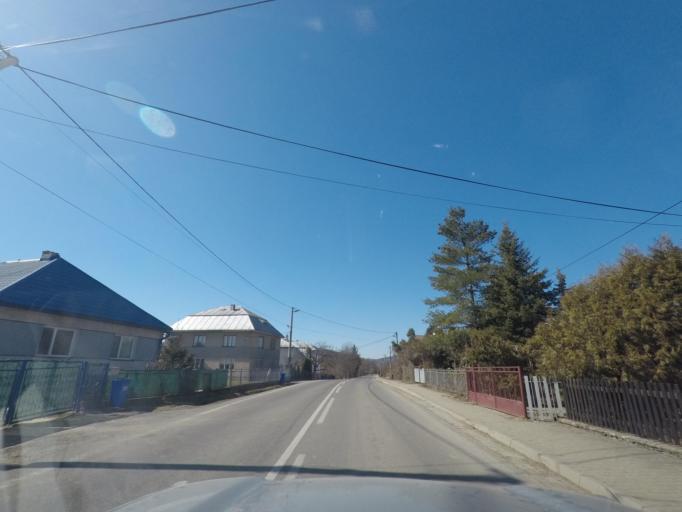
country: UA
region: Zakarpattia
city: Velykyi Bereznyi
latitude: 48.8937
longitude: 22.4074
